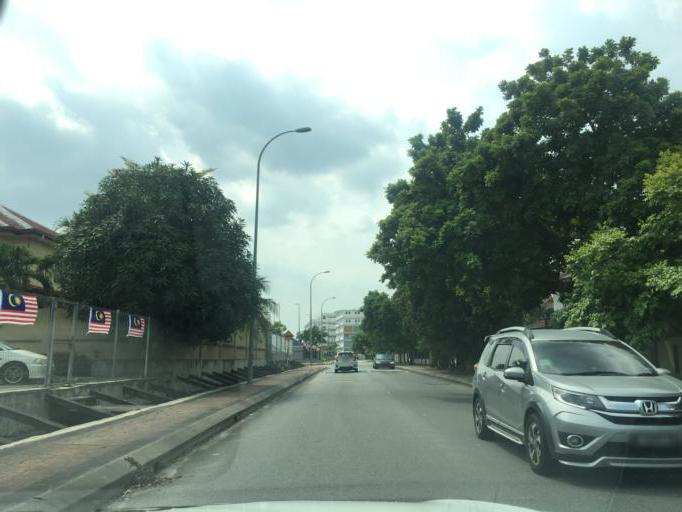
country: MY
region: Selangor
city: Shah Alam
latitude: 3.0764
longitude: 101.4883
